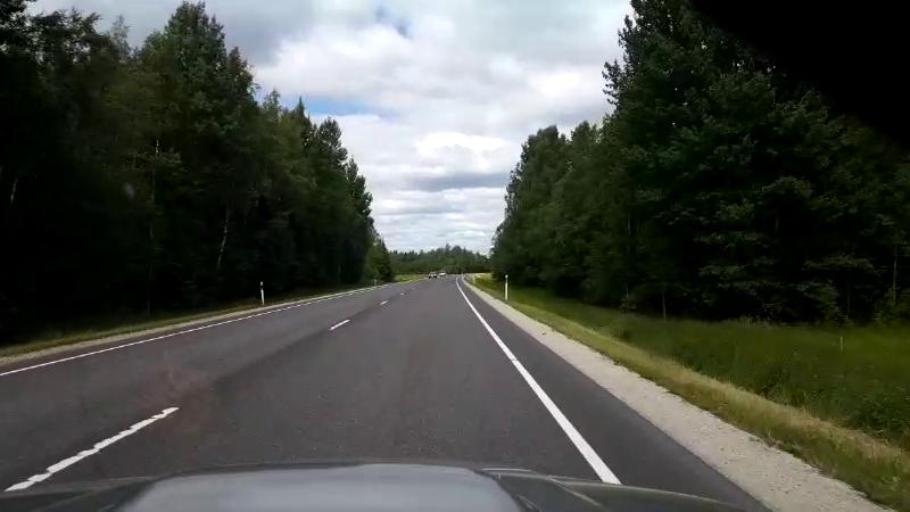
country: EE
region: Raplamaa
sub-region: Maerjamaa vald
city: Marjamaa
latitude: 58.8188
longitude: 24.4128
